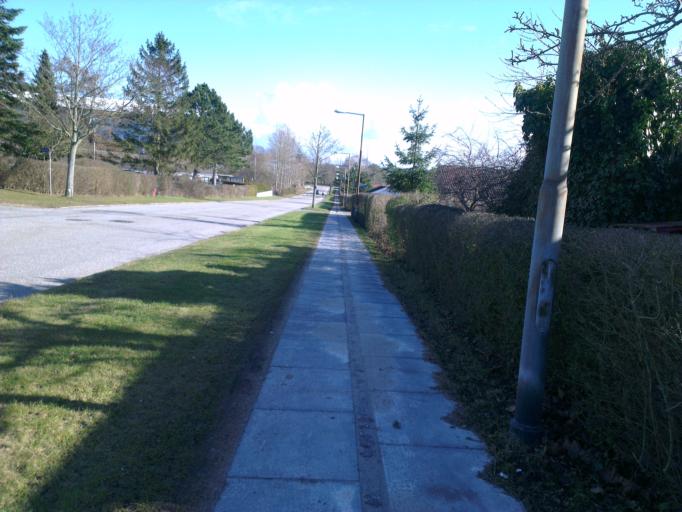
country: DK
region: Capital Region
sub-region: Frederikssund Kommune
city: Frederikssund
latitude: 55.8471
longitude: 12.0556
